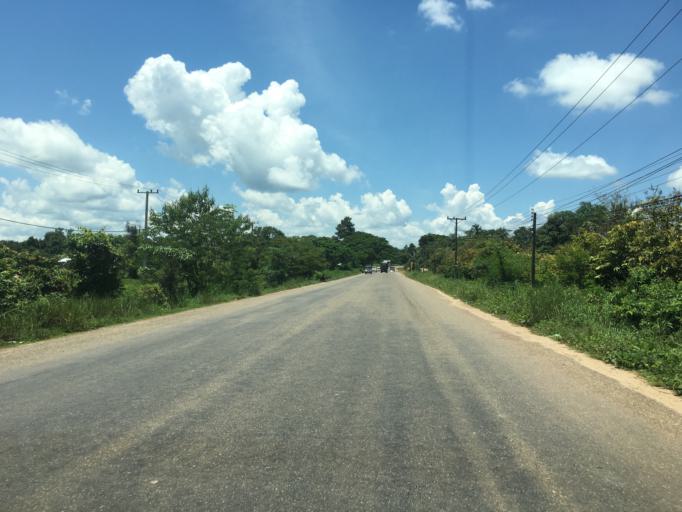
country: LA
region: Vientiane
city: Muang Phon-Hong
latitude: 18.2377
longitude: 102.4868
